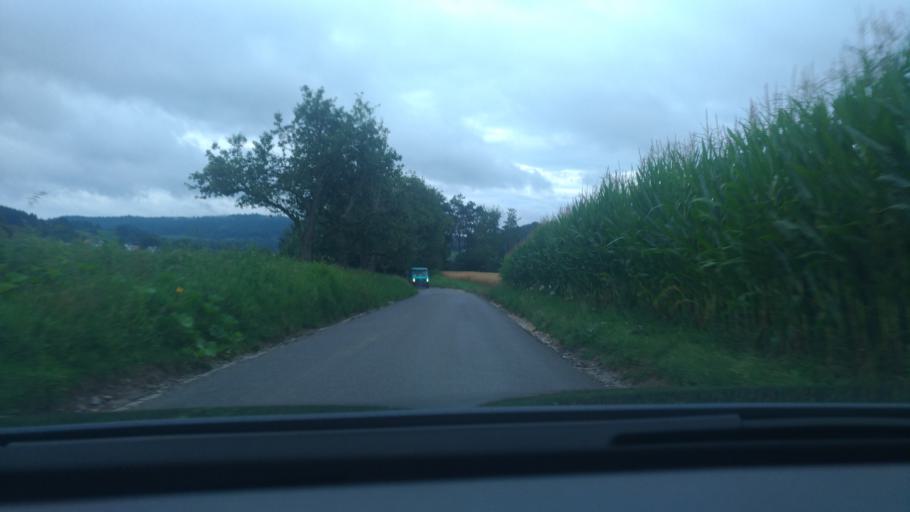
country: DE
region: Baden-Wuerttemberg
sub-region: Freiburg Region
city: Bodman-Ludwigshafen
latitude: 47.8420
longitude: 9.0923
